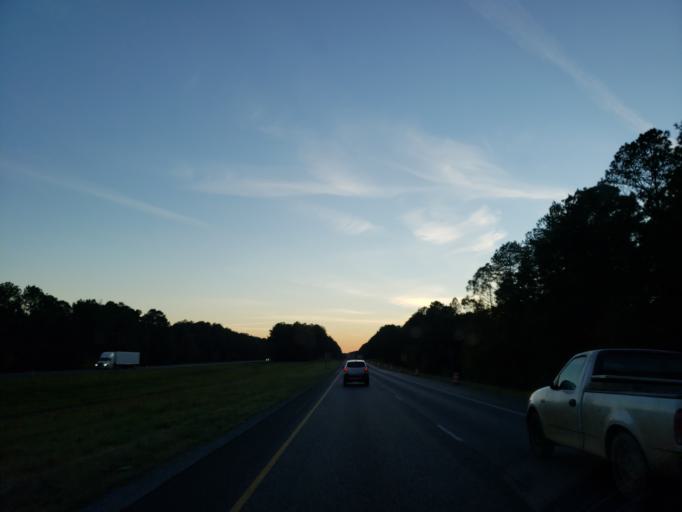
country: US
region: Alabama
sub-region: Sumter County
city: York
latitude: 32.5497
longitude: -88.2715
